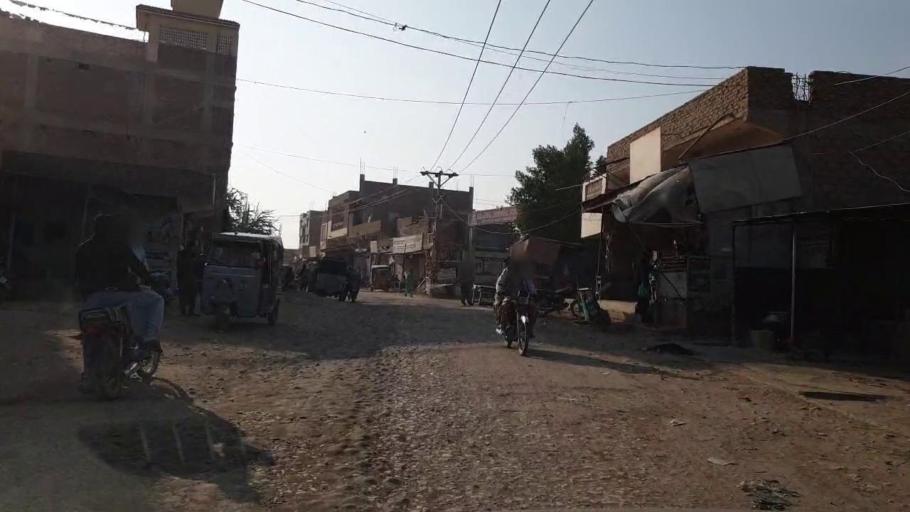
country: PK
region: Sindh
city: Kotri
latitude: 25.3593
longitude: 68.2749
